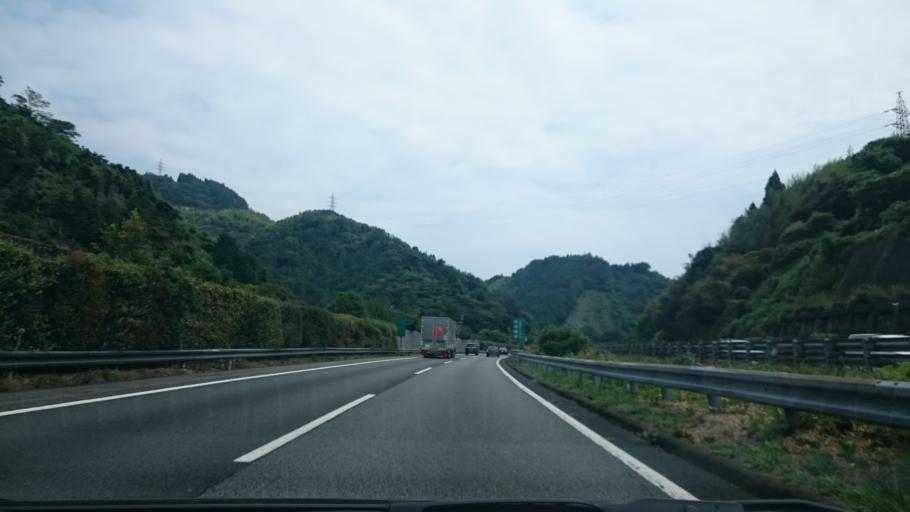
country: JP
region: Shizuoka
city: Fujinomiya
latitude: 35.0682
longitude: 138.5318
